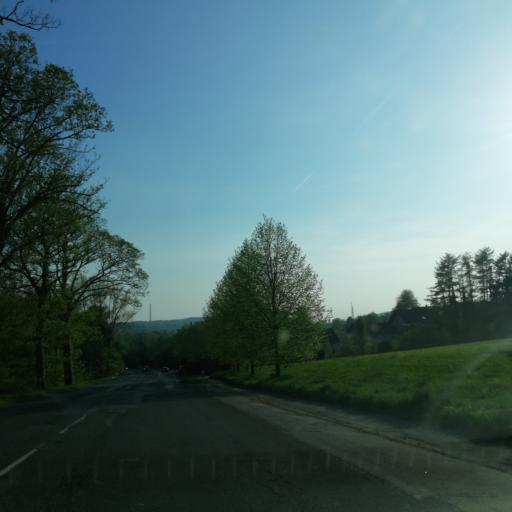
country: DE
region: North Rhine-Westphalia
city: Herdecke
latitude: 51.4278
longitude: 7.4433
